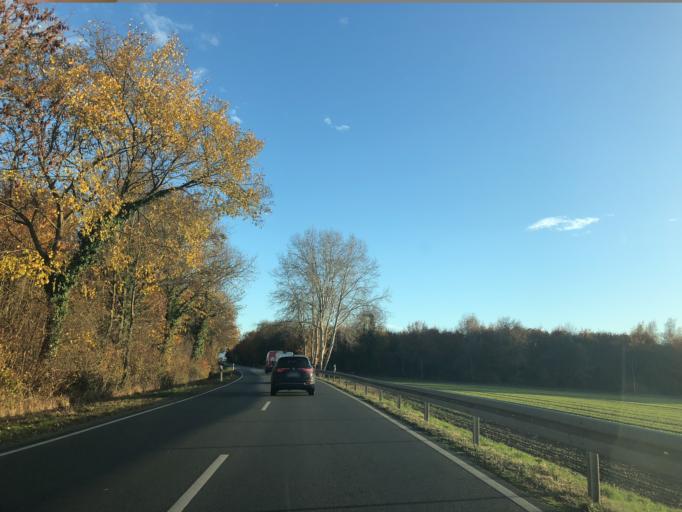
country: DE
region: Hesse
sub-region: Regierungsbezirk Darmstadt
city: Buttelborn
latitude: 49.8808
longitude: 8.5310
